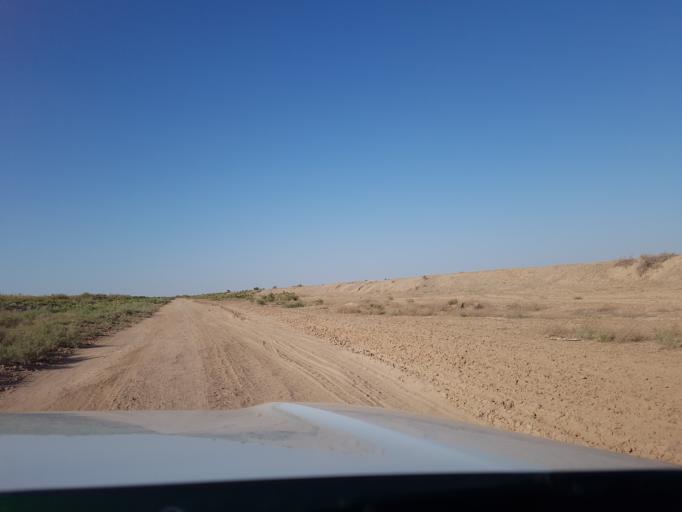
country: IR
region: Razavi Khorasan
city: Sarakhs
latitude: 36.9725
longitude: 61.3841
